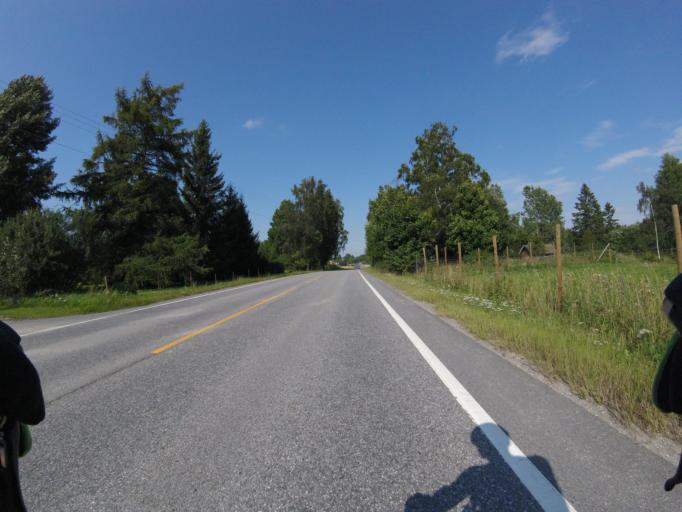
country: NO
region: Akershus
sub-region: Sorum
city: Frogner
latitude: 60.0468
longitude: 11.1185
